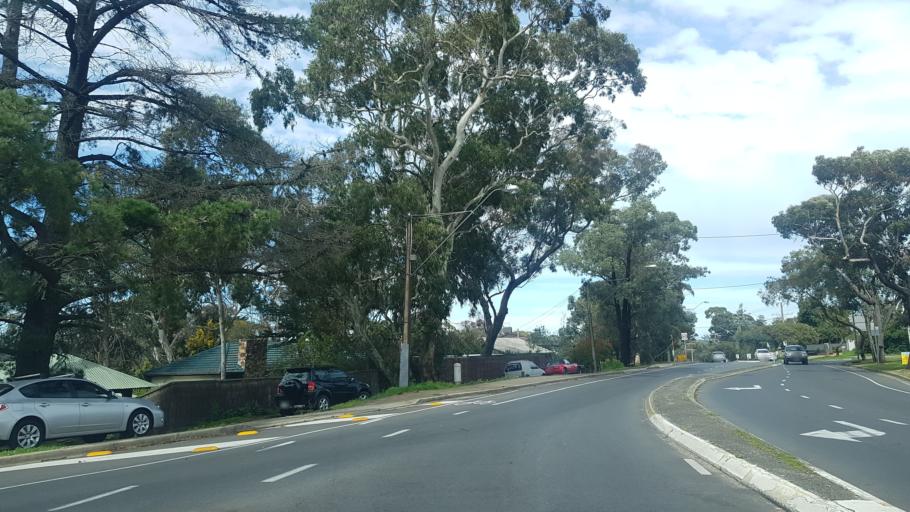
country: AU
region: South Australia
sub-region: Mitcham
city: Belair
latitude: -34.9988
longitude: 138.6232
